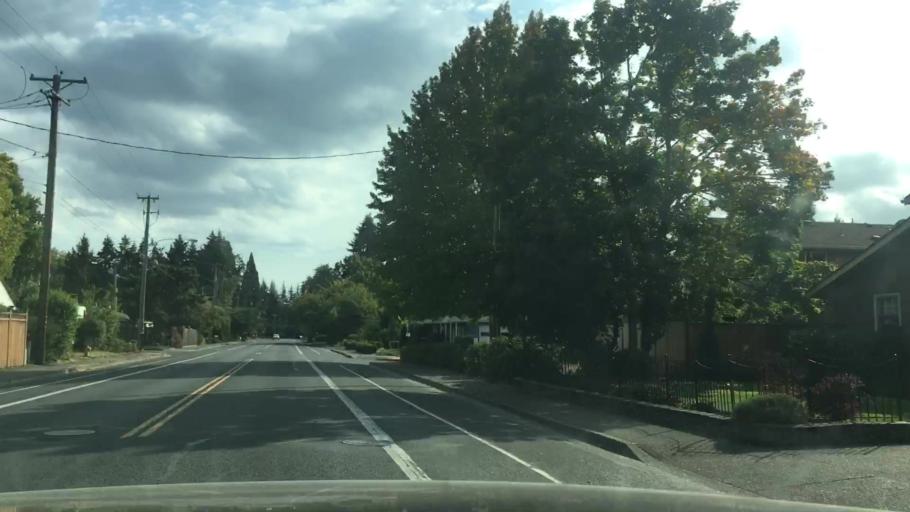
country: US
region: Oregon
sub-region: Lane County
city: Eugene
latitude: 44.0867
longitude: -123.0881
